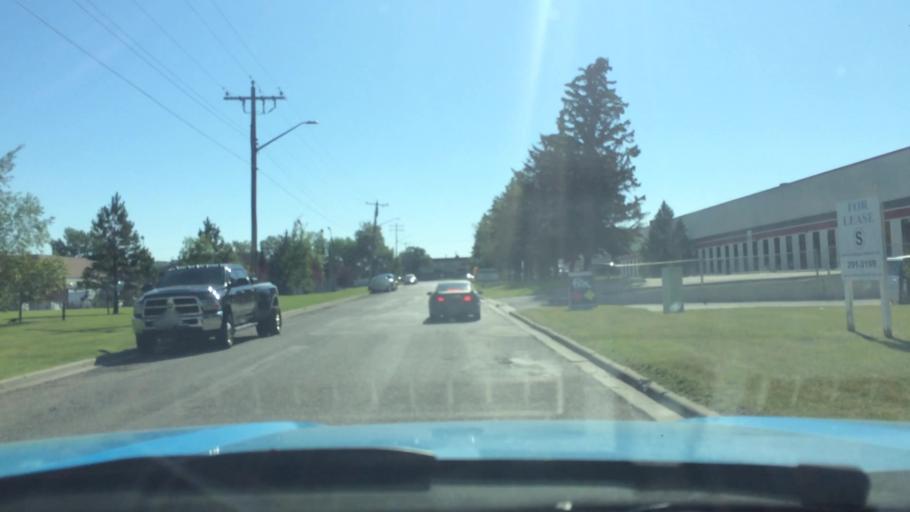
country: CA
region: Alberta
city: Calgary
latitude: 51.0899
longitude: -114.0084
